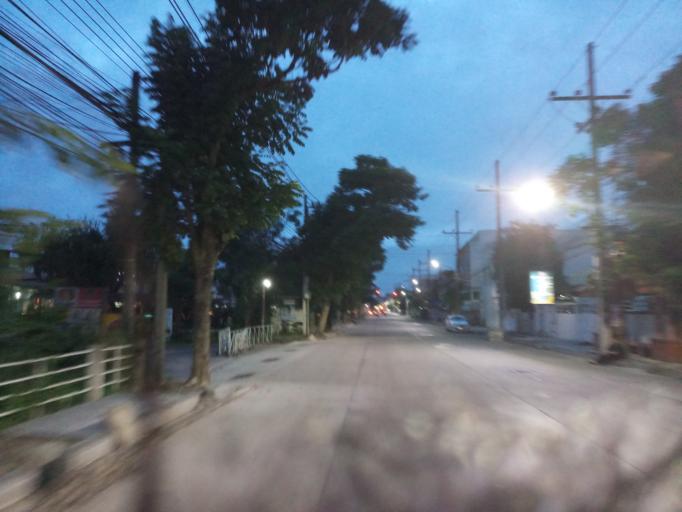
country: TH
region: Chiang Rai
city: Chiang Rai
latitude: 19.8997
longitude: 99.8323
